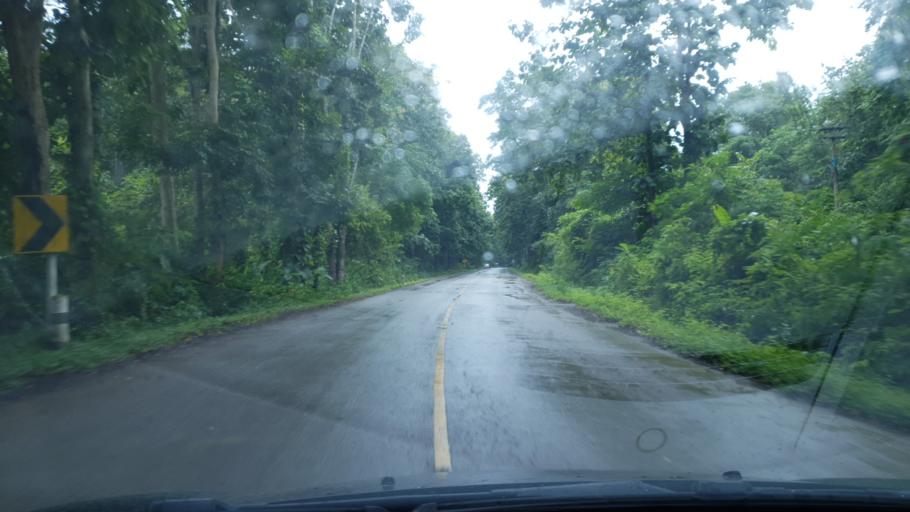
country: TH
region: Mae Hong Son
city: Pa Pae
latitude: 18.2511
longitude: 97.9433
